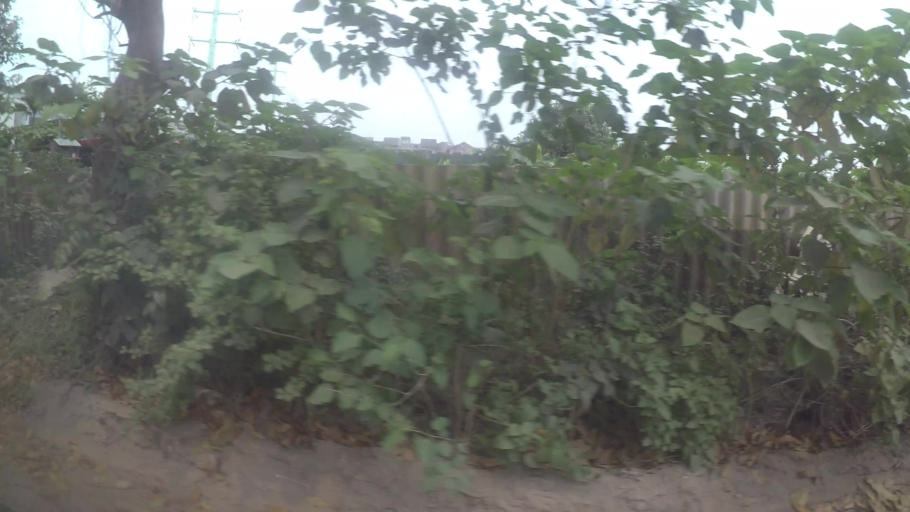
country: VN
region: Ha Noi
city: Cau Dien
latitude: 21.0241
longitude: 105.7424
